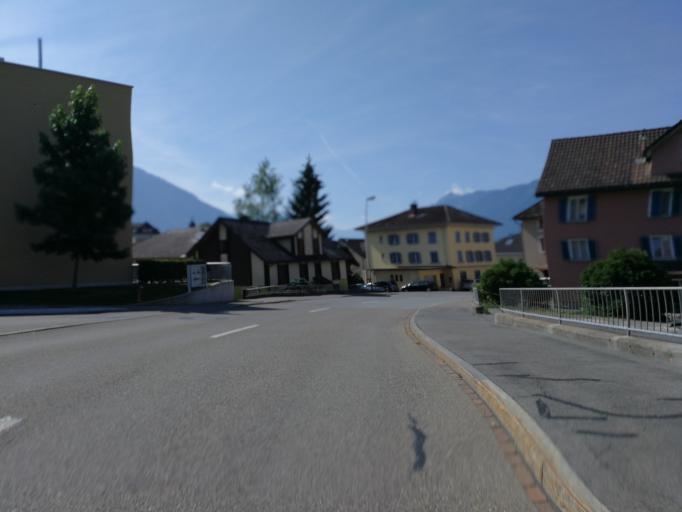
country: CH
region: Saint Gallen
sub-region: Wahlkreis See-Gaster
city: Kaltbrunn
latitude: 47.2158
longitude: 9.0272
